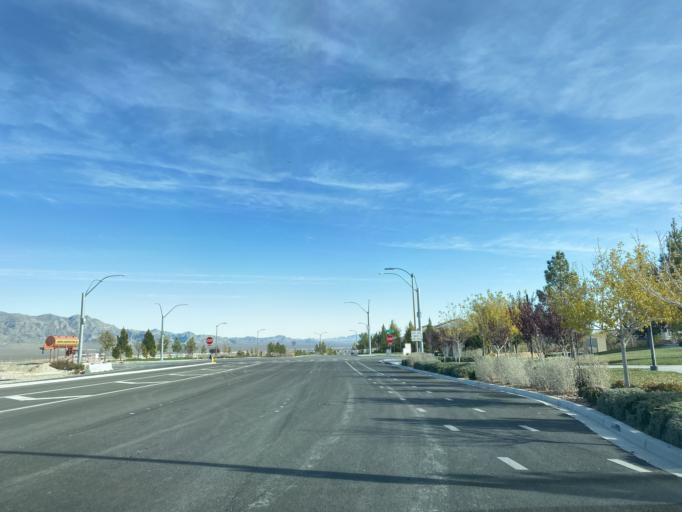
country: US
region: Nevada
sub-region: Clark County
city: Summerlin South
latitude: 36.3140
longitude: -115.3159
